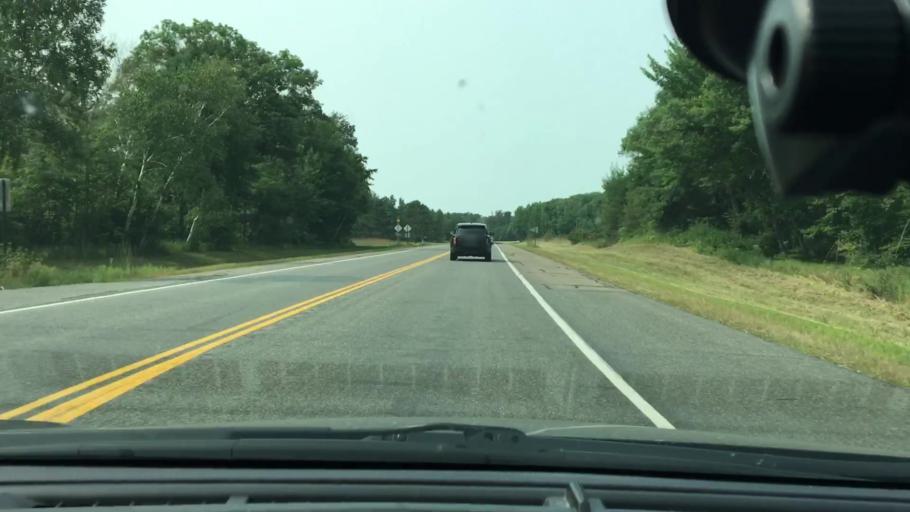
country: US
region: Minnesota
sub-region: Crow Wing County
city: Breezy Point
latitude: 46.4851
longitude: -94.1610
